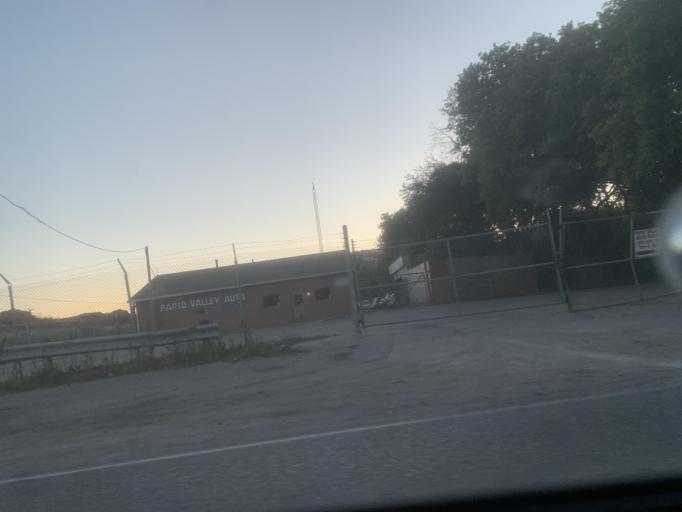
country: US
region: Nebraska
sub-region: Sarpy County
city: La Vista
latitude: 41.1981
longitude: -96.0065
